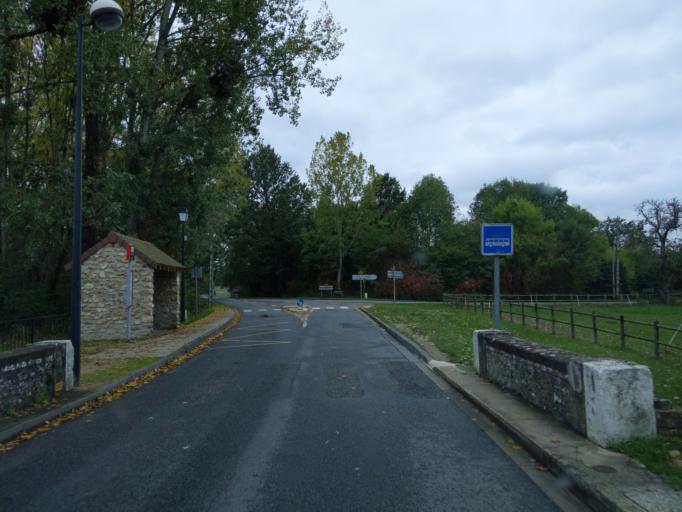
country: FR
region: Ile-de-France
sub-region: Departement des Yvelines
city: Bullion
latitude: 48.6220
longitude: 1.9929
